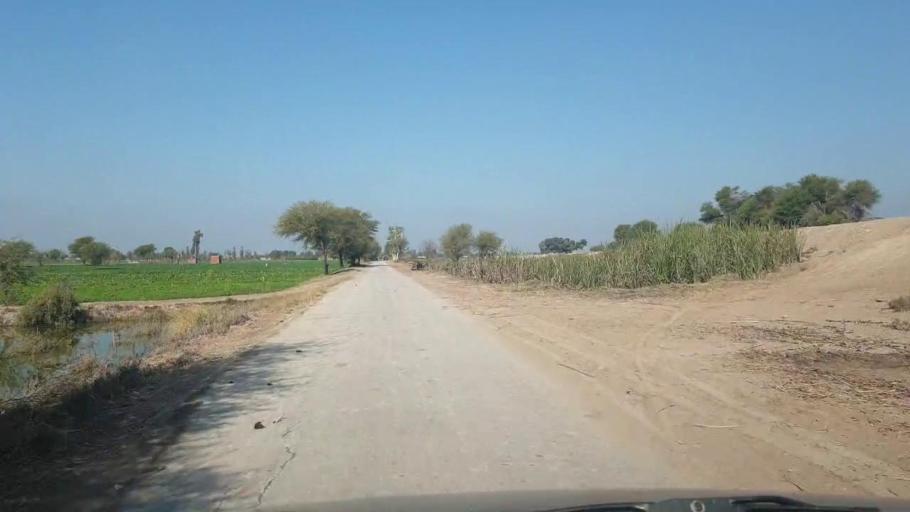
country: PK
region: Sindh
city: Shahdadpur
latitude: 25.8829
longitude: 68.5451
